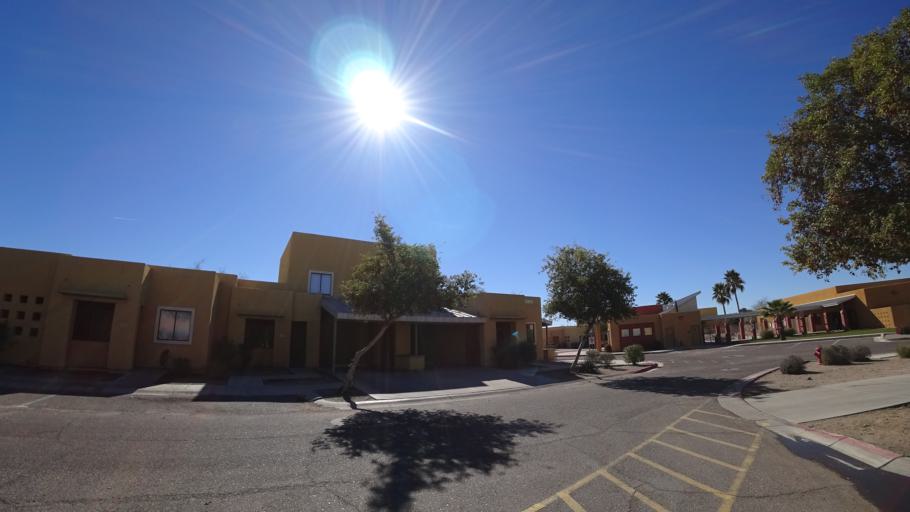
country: US
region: Arizona
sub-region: Maricopa County
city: Avondale
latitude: 33.4269
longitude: -112.3427
